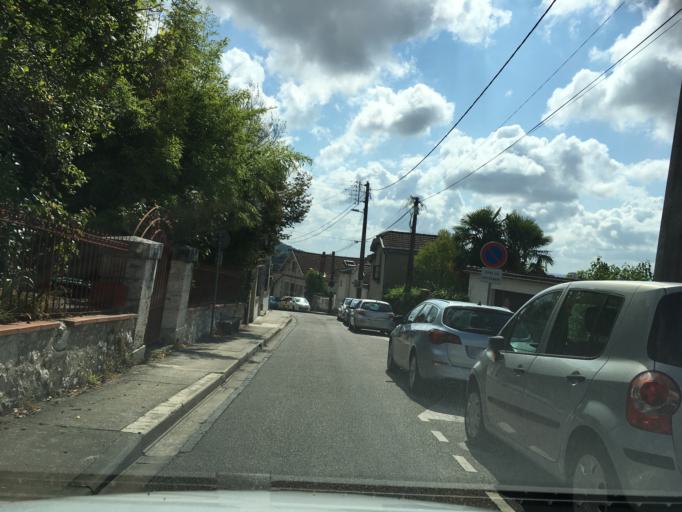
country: FR
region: Aquitaine
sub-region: Departement du Lot-et-Garonne
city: Agen
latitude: 44.2100
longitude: 0.6207
